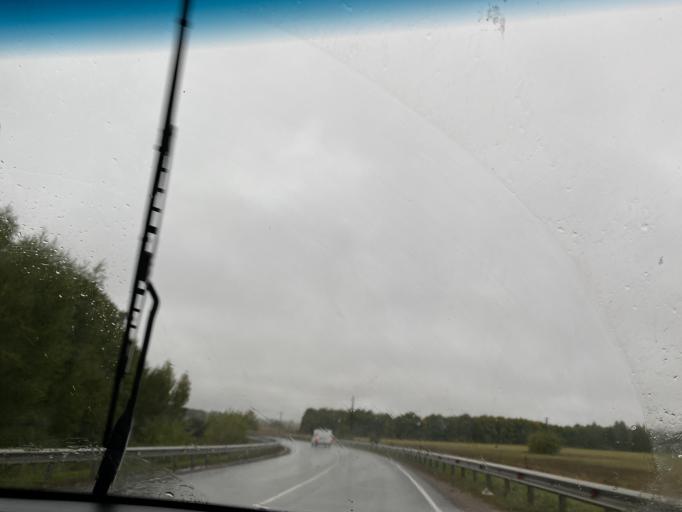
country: RU
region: Rjazan
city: Murmino
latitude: 54.4600
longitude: 39.8782
